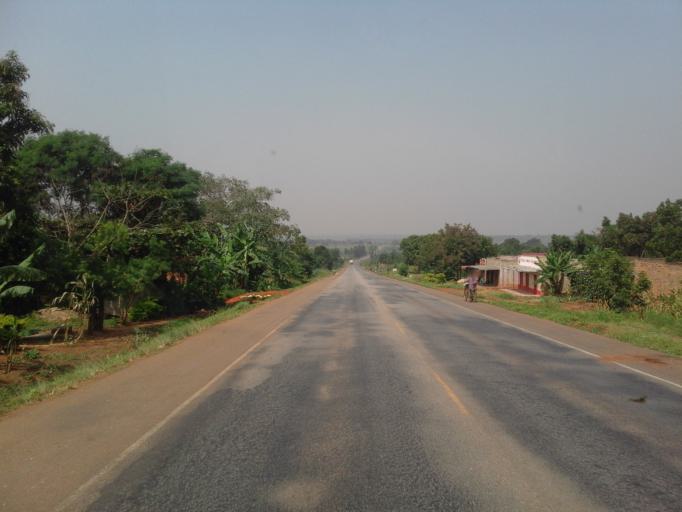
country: UG
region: Eastern Region
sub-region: Iganga District
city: Iganga
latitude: 0.6313
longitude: 33.5715
